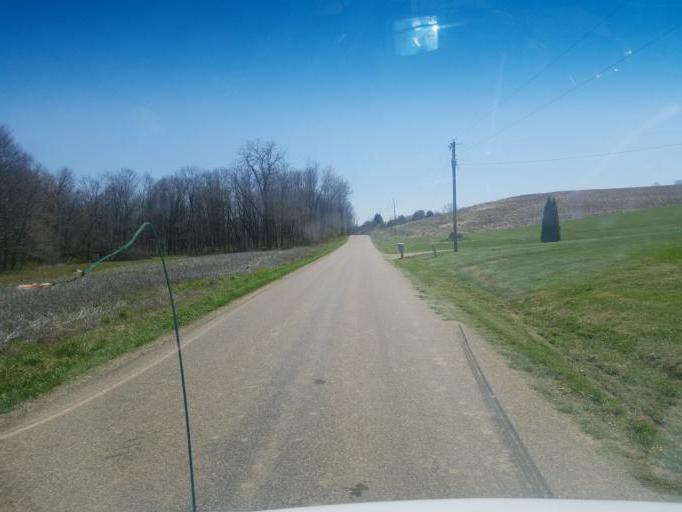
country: US
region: Ohio
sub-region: Knox County
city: Oak Hill
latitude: 40.3849
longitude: -82.3160
